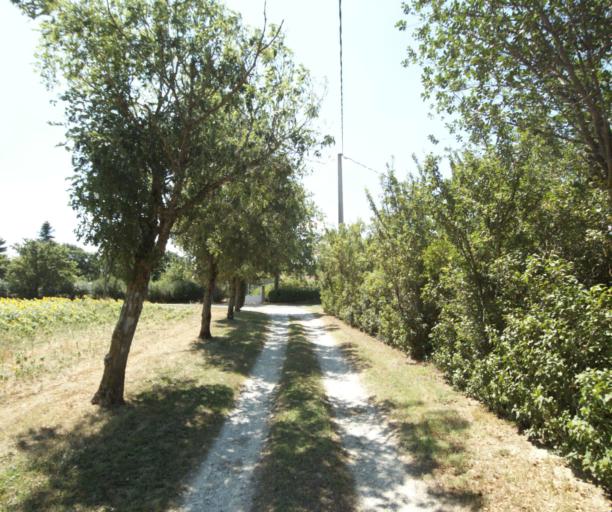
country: FR
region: Midi-Pyrenees
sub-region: Departement de la Haute-Garonne
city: Saint-Felix-Lauragais
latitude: 43.4766
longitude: 1.8584
